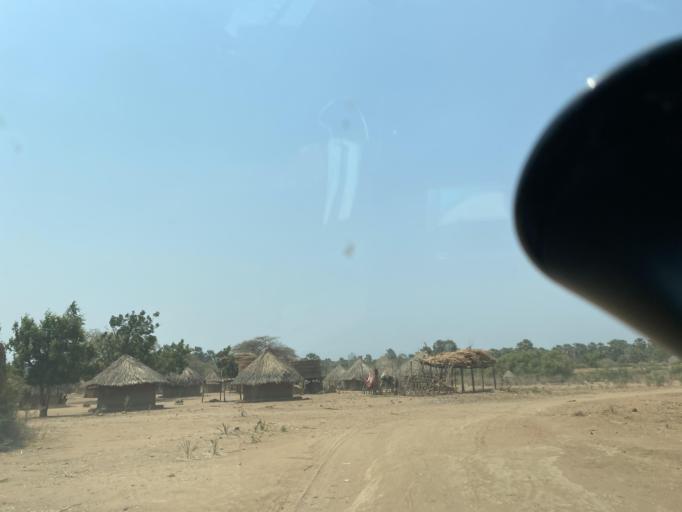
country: ZW
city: Chirundu
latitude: -16.1535
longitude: 28.8060
